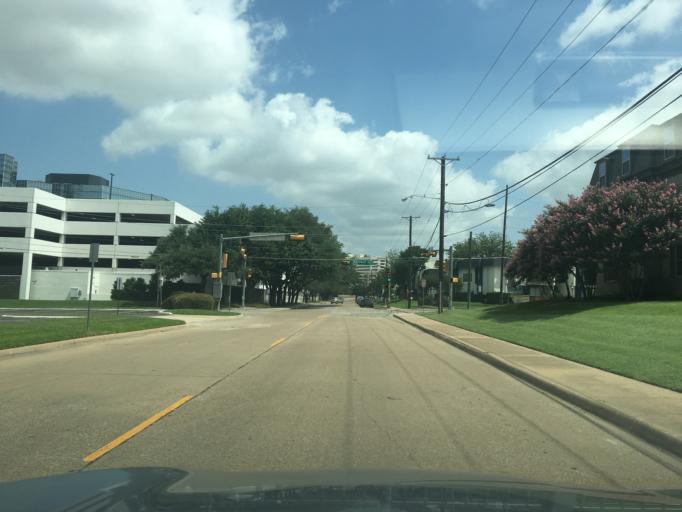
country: US
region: Texas
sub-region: Dallas County
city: Addison
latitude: 32.9215
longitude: -96.8151
